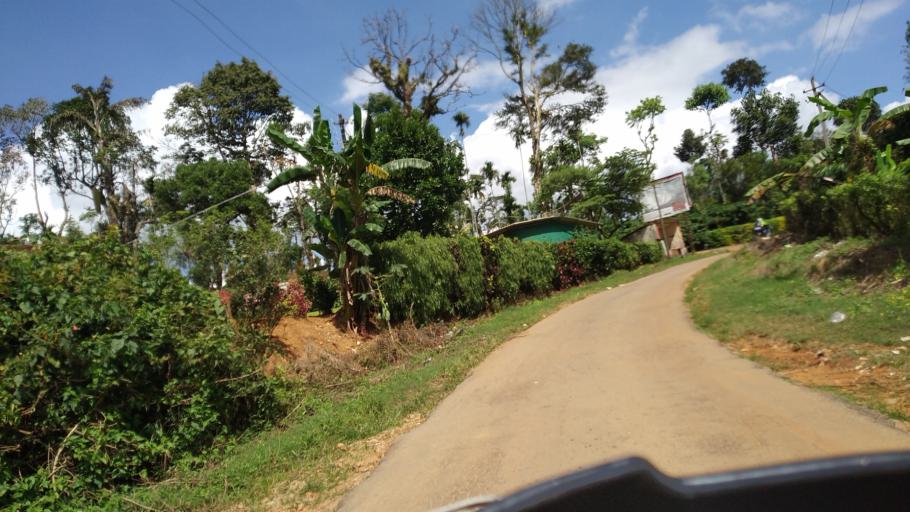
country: IN
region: Karnataka
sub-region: Kodagu
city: Ponnampet
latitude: 12.0307
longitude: 75.8976
